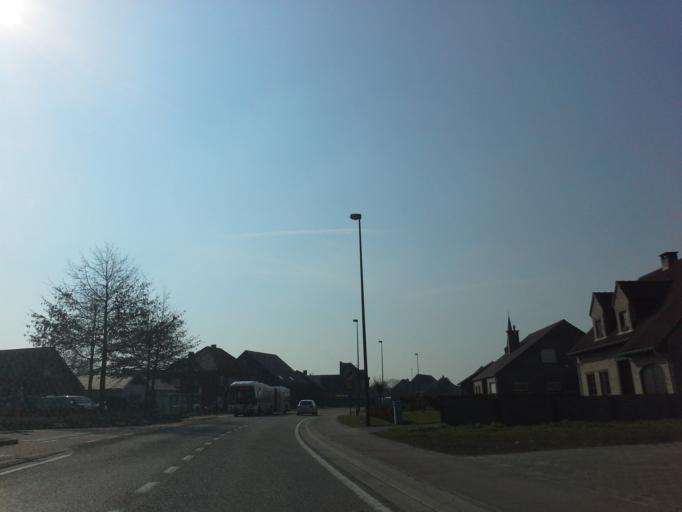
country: BE
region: Flanders
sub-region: Provincie Limburg
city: Tessenderlo
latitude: 51.0858
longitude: 5.1064
